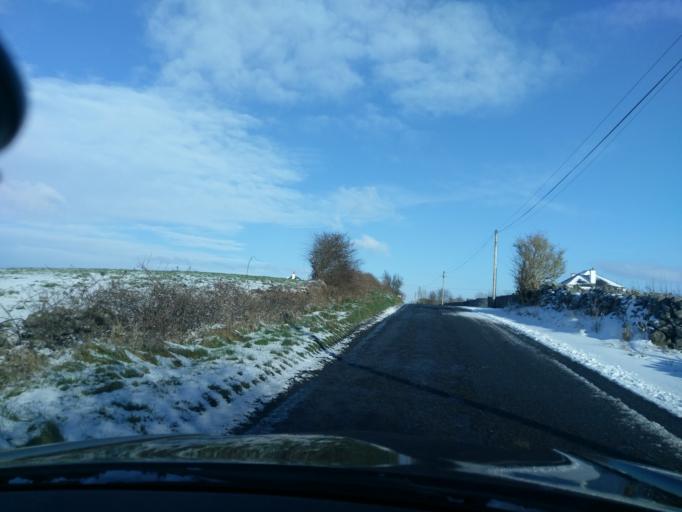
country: IE
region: Connaught
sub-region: County Galway
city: Athenry
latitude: 53.1990
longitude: -8.8159
